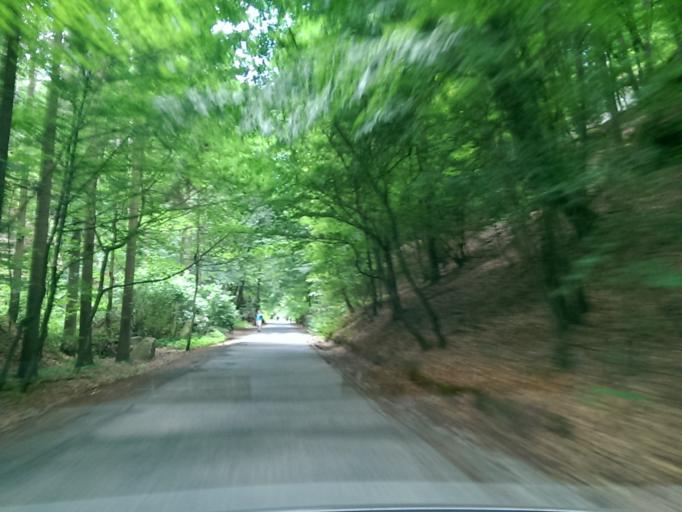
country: CZ
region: Central Bohemia
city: Mseno
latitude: 50.4396
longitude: 14.5790
